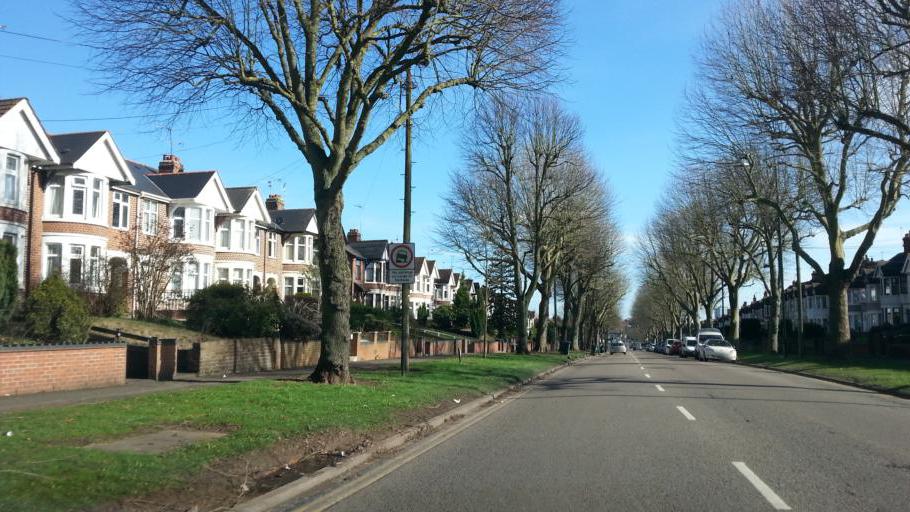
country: GB
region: England
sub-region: Coventry
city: Coventry
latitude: 52.4159
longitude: -1.5368
